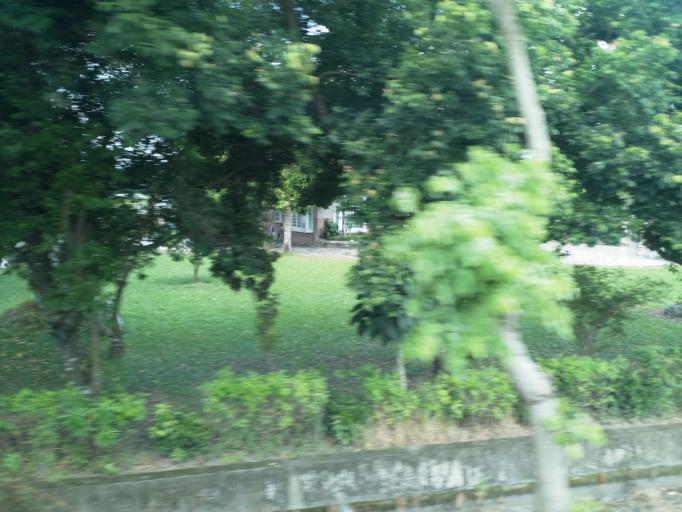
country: TW
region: Taiwan
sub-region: Pingtung
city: Pingtung
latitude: 22.8858
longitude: 120.5537
